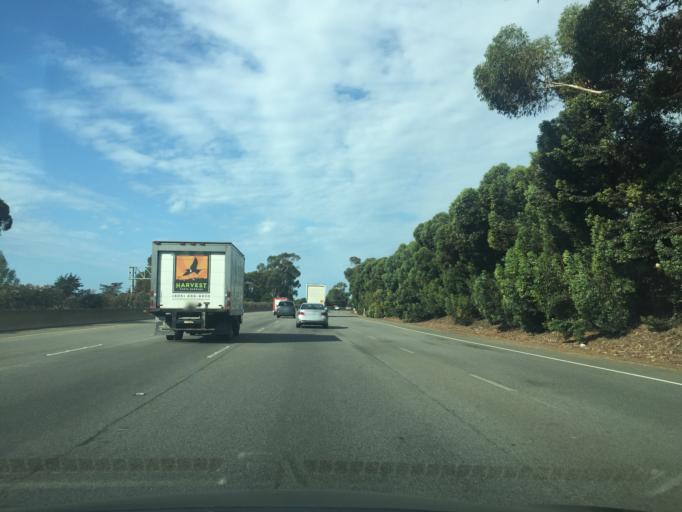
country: US
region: California
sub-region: Santa Barbara County
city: Goleta
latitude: 34.4421
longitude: -119.7924
